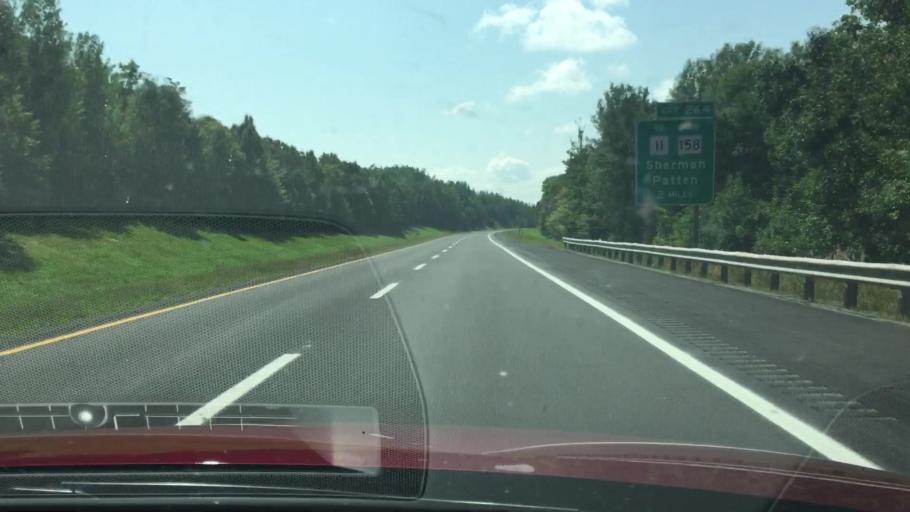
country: US
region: Maine
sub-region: Penobscot County
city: Patten
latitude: 45.9084
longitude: -68.3819
